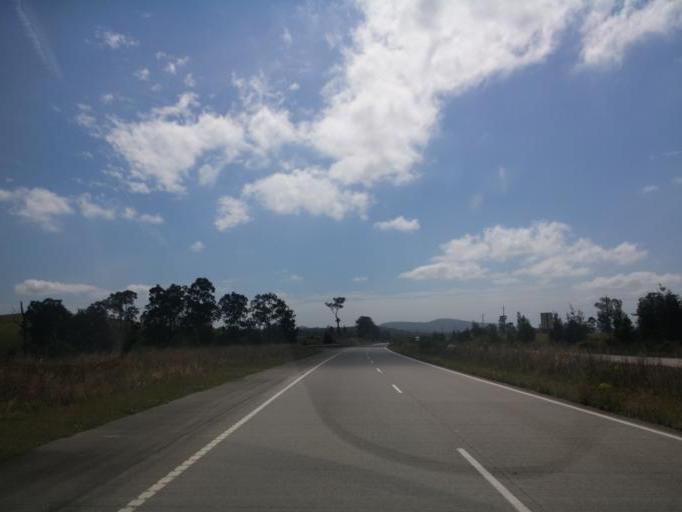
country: AU
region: New South Wales
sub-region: Great Lakes
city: Hawks Nest
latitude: -32.5729
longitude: 152.1307
